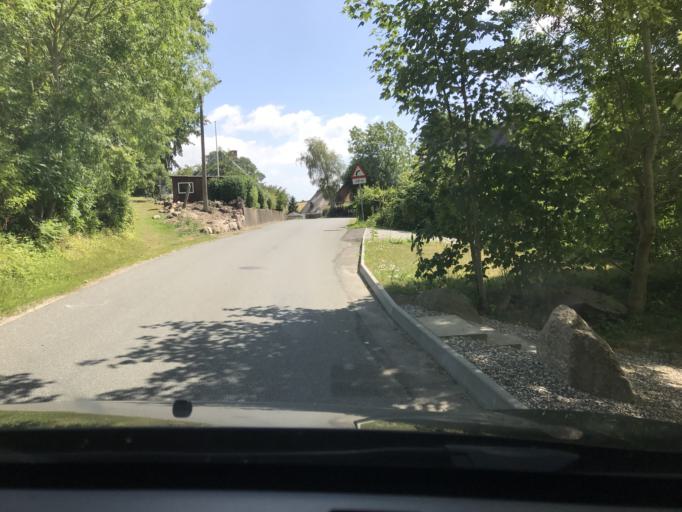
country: DK
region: South Denmark
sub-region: AEro Kommune
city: AEroskobing
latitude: 54.9108
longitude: 10.3023
